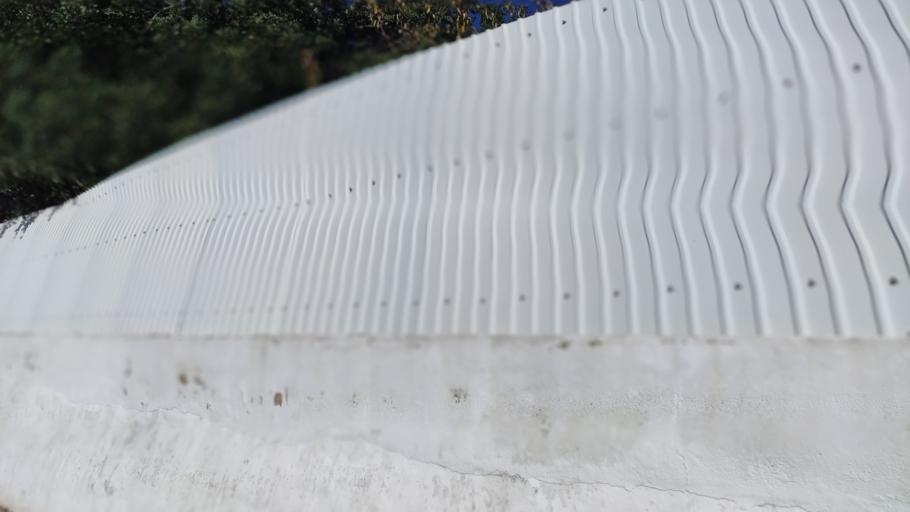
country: PT
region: Faro
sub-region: Sao Bras de Alportel
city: Sao Bras de Alportel
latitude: 37.1532
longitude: -7.9072
